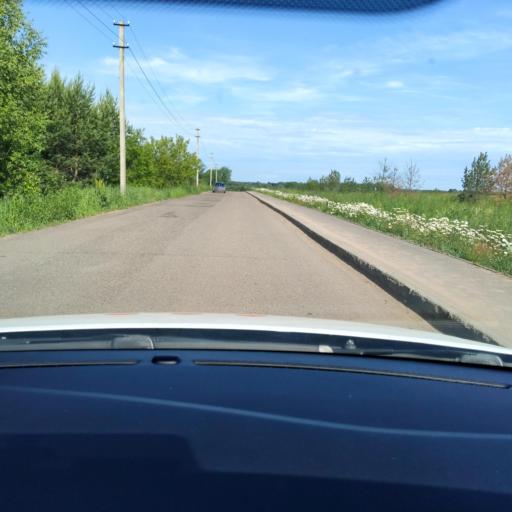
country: RU
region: Tatarstan
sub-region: Gorod Kazan'
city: Kazan
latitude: 55.8911
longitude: 49.0925
